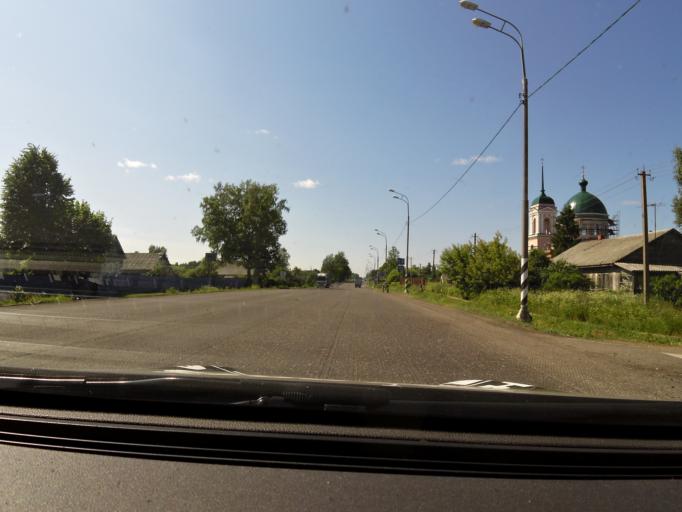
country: RU
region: Novgorod
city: Proletariy
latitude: 58.3681
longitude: 32.0619
